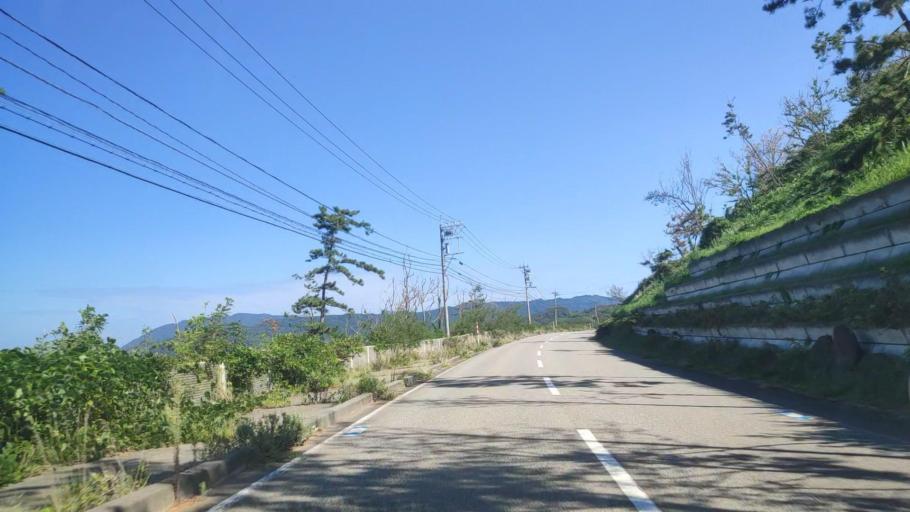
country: JP
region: Ishikawa
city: Nanao
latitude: 37.2698
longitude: 136.7296
